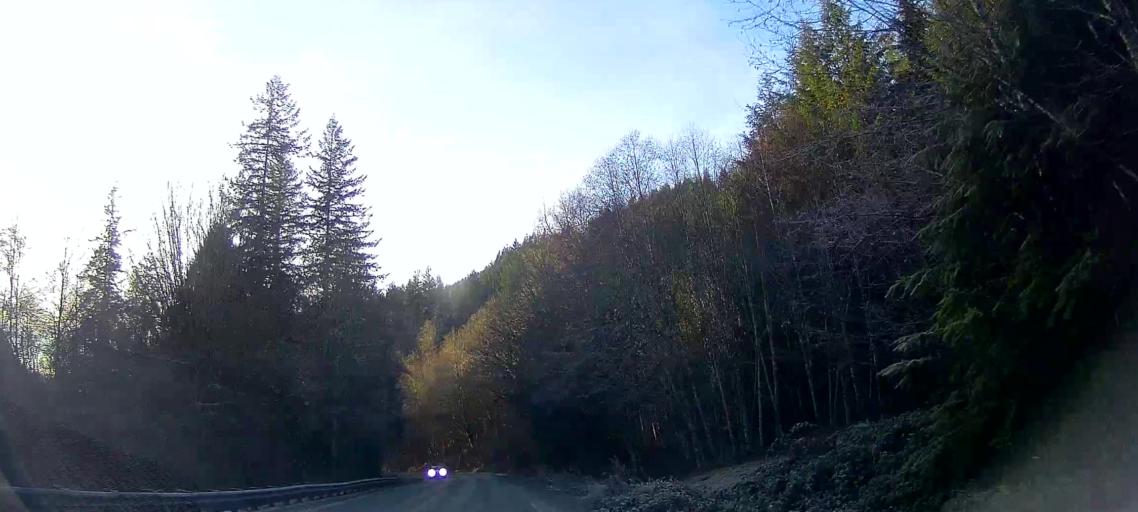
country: US
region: Washington
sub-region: Snohomish County
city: Darrington
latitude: 48.5610
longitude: -121.8352
